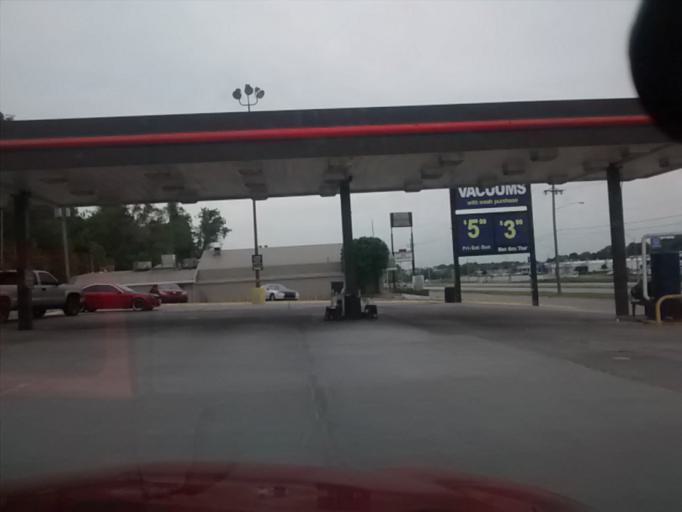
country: US
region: Nebraska
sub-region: Sarpy County
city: Bellevue
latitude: 41.1705
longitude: -95.9248
